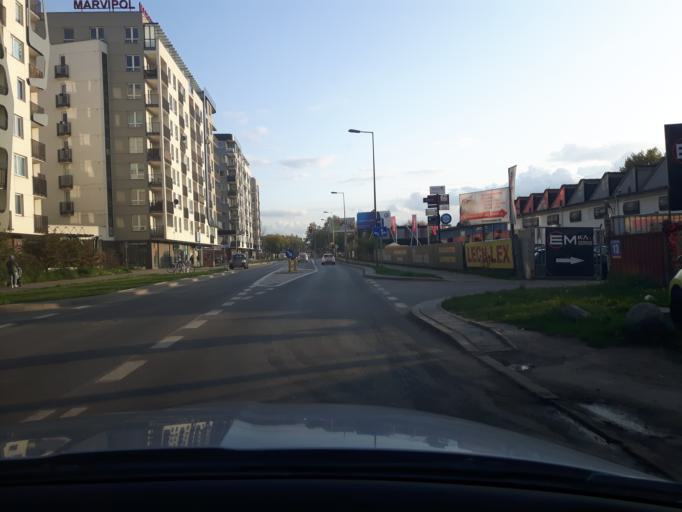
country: PL
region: Masovian Voivodeship
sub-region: Warszawa
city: Wlochy
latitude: 52.1642
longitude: 20.9922
